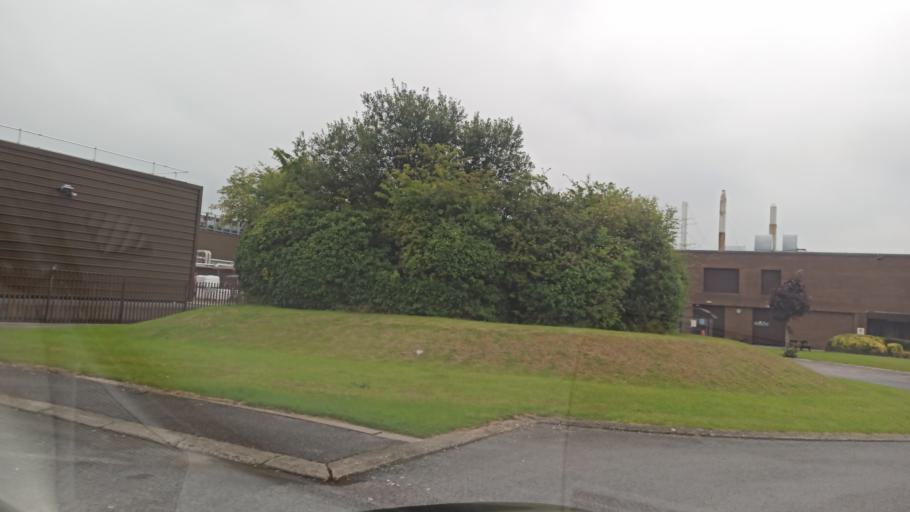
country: IE
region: Munster
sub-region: South Tipperary
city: Cluain Meala
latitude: 52.3724
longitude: -7.7243
